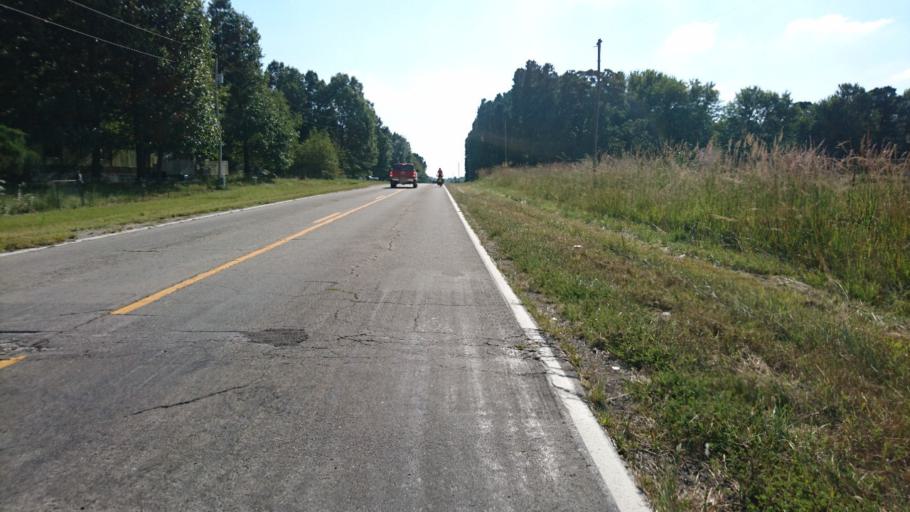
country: US
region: Missouri
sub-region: Laclede County
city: Lebanon
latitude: 37.6139
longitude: -92.6981
